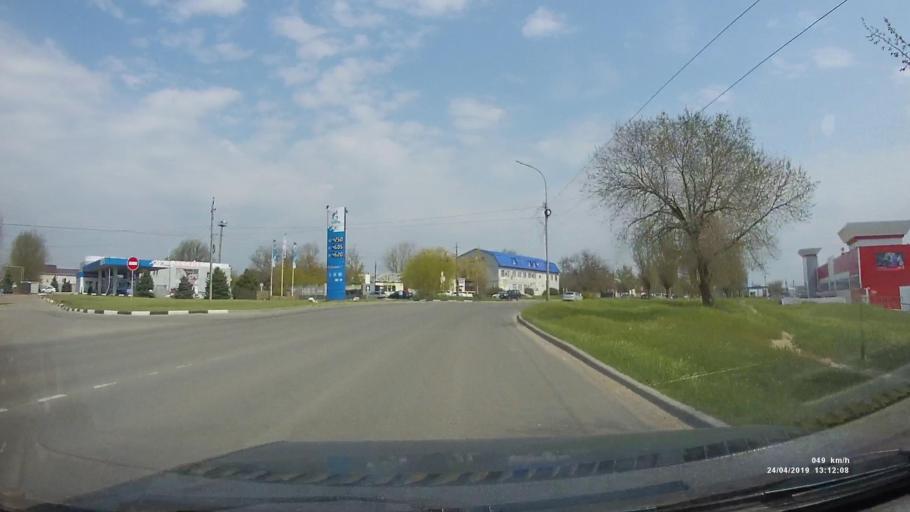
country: RU
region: Kalmykiya
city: Elista
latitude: 46.3133
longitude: 44.3012
